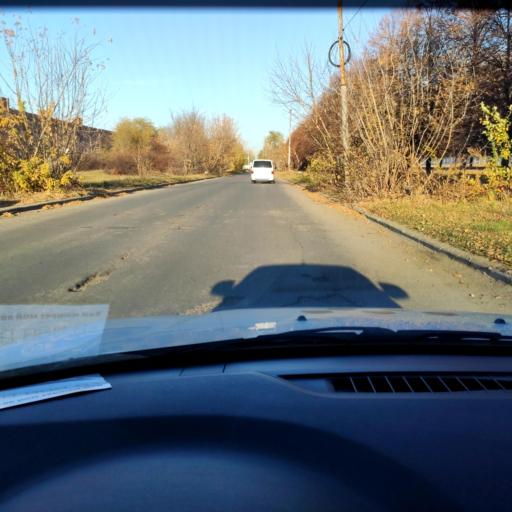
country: RU
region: Samara
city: Tol'yatti
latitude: 53.5388
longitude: 49.3082
